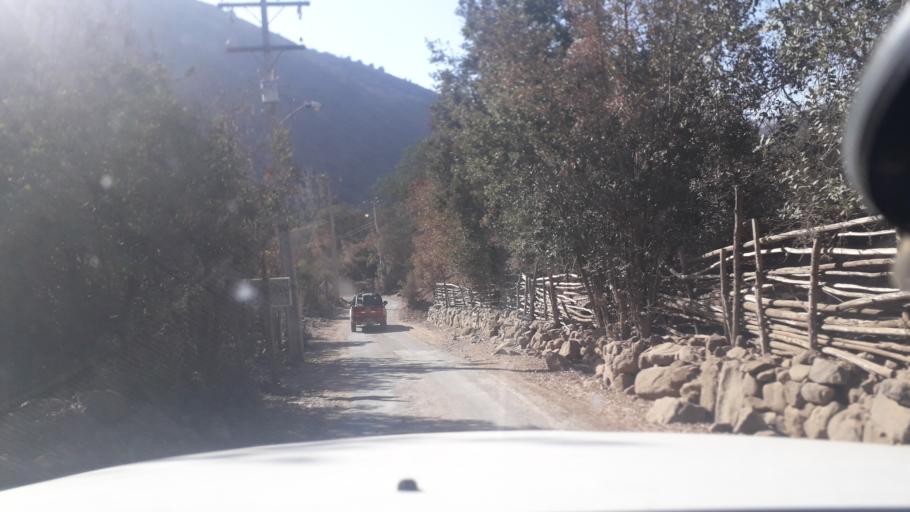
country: CL
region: Valparaiso
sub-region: Provincia de Marga Marga
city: Limache
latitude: -33.0737
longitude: -71.0994
